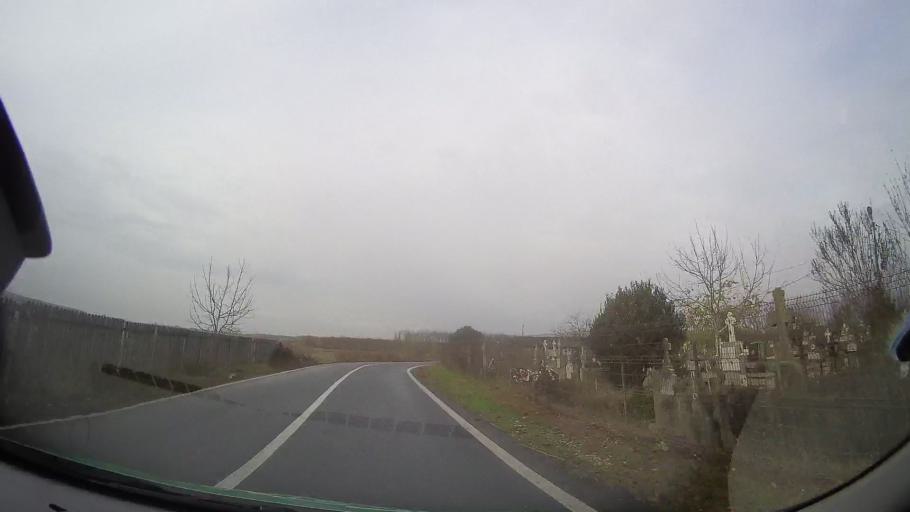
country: RO
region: Ialomita
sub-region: Comuna Fierbinti-Targ
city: Fierbinti-Targ
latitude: 44.6733
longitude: 26.3506
